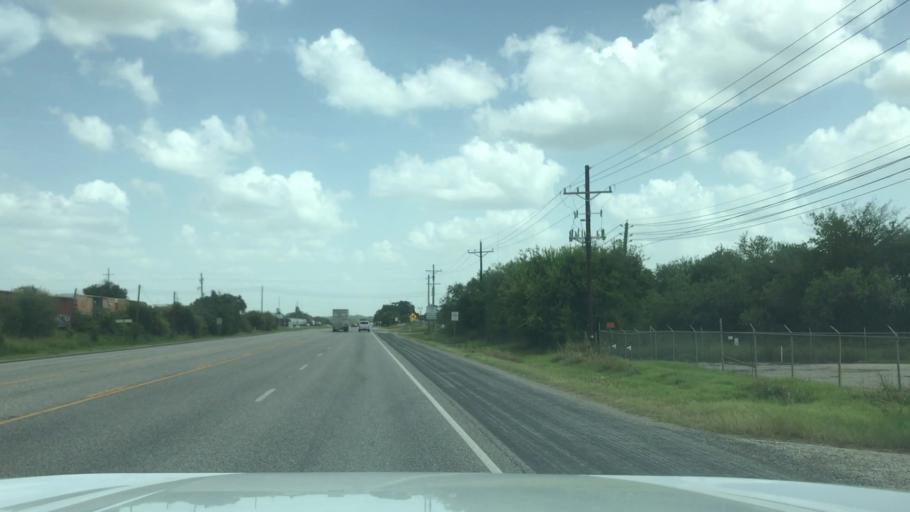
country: US
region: Texas
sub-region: Robertson County
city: Hearne
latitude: 30.8585
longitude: -96.5767
